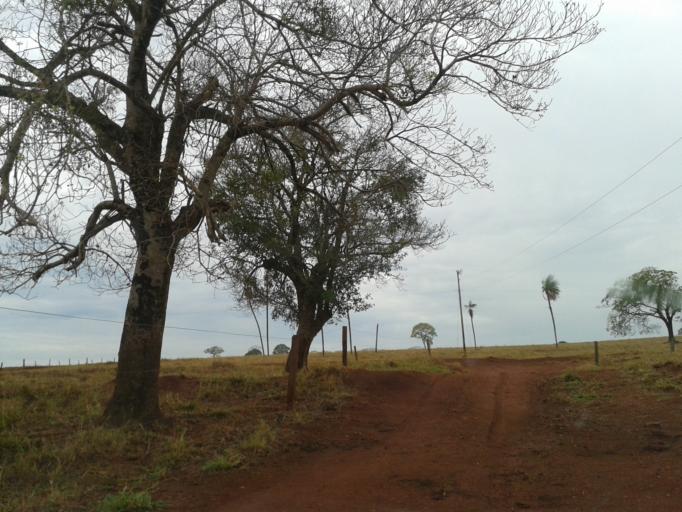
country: BR
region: Minas Gerais
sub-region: Santa Vitoria
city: Santa Vitoria
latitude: -18.8501
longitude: -49.8297
